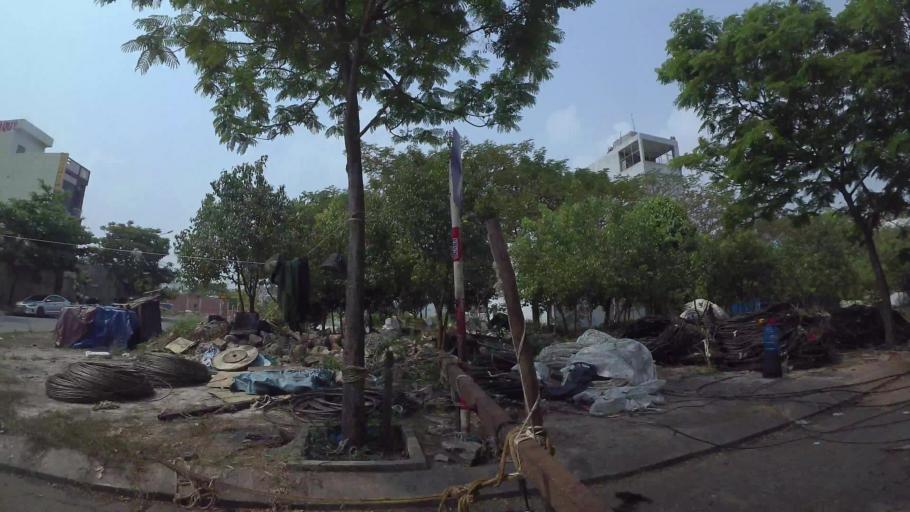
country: VN
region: Da Nang
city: Da Nang
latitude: 16.0916
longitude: 108.2392
